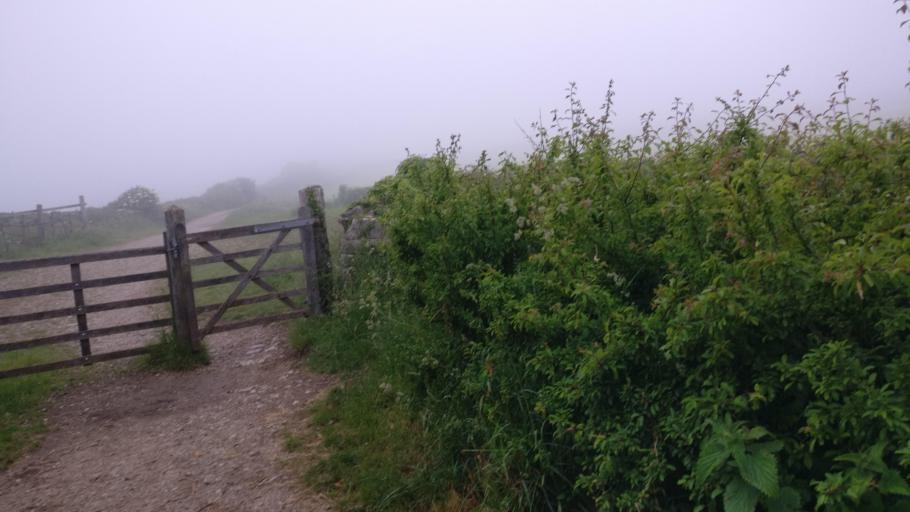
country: GB
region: England
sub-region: Dorset
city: Swanage
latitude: 50.6011
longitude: -2.0206
